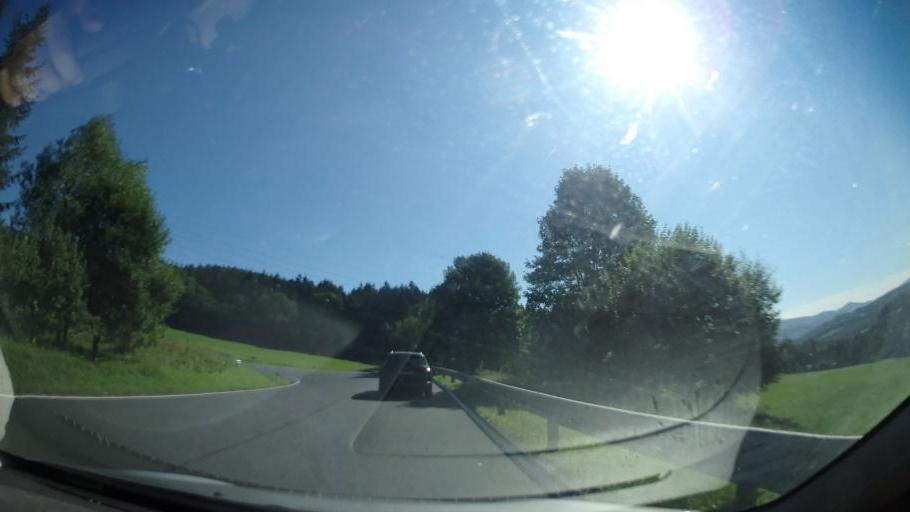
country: CZ
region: Olomoucky
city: Vapenna
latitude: 50.2419
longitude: 17.1436
